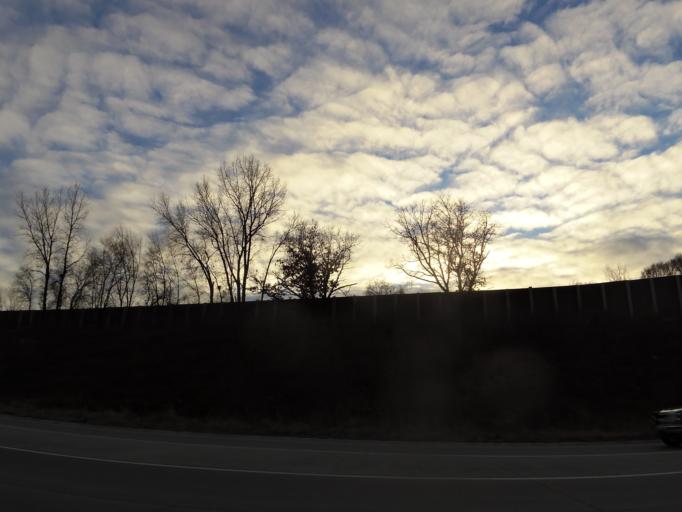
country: US
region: Minnesota
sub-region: Ramsey County
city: Little Canada
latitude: 45.0468
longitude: -93.1095
